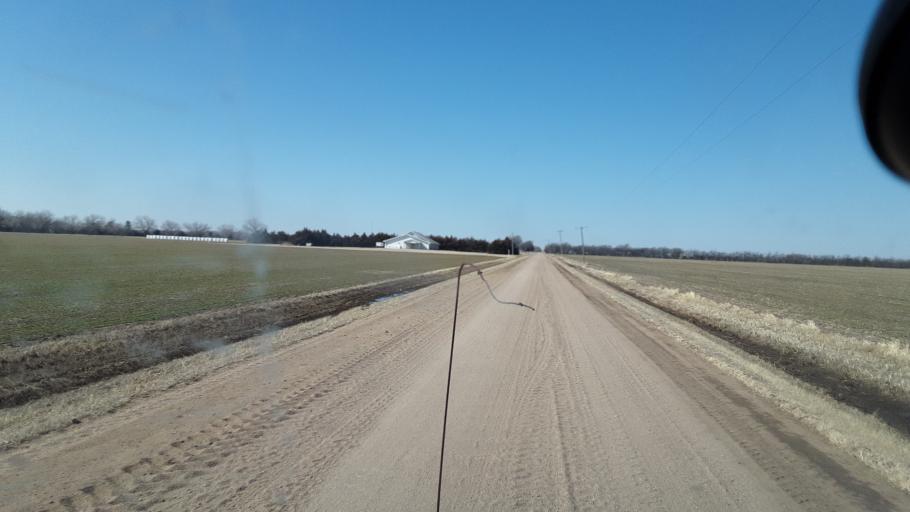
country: US
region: Kansas
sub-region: Reno County
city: South Hutchinson
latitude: 37.9846
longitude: -98.0191
